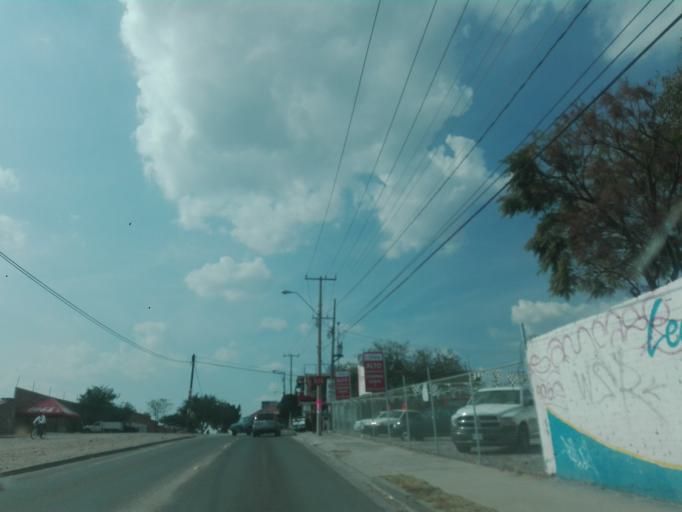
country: MX
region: Guanajuato
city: Leon
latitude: 21.1749
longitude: -101.6756
